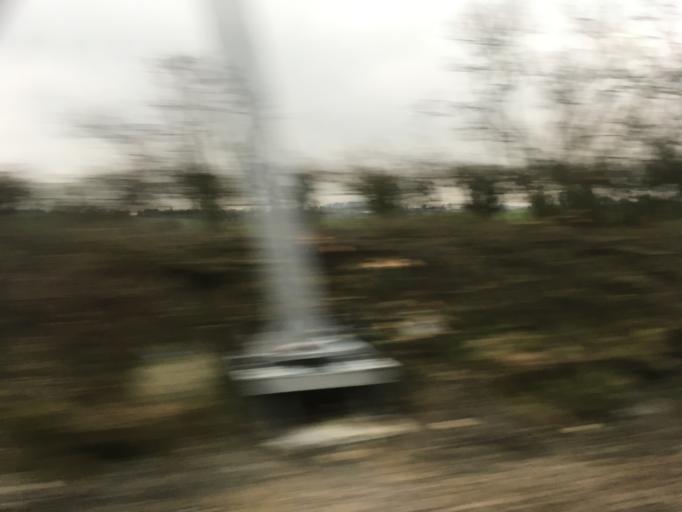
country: GB
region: England
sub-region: Wiltshire
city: Norton
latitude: 51.5453
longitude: -2.1566
